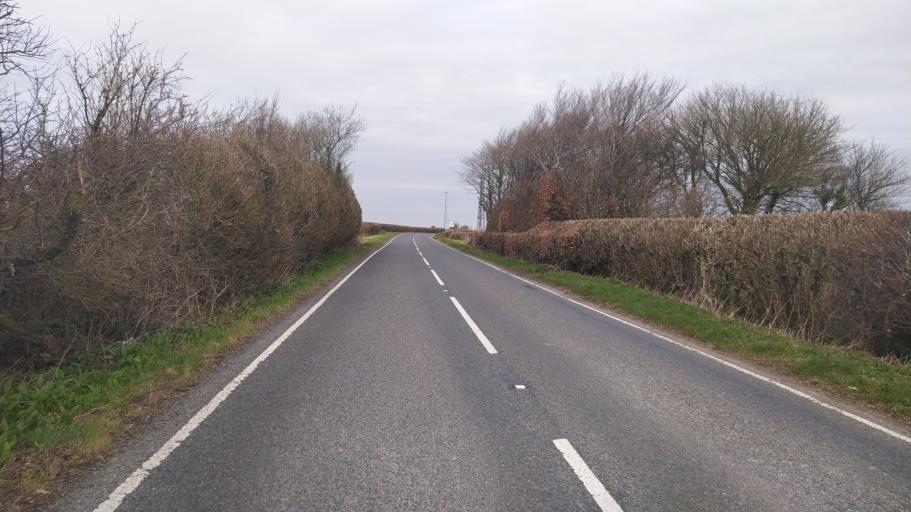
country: GB
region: England
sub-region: Dorset
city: Beaminster
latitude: 50.8398
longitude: -2.7063
